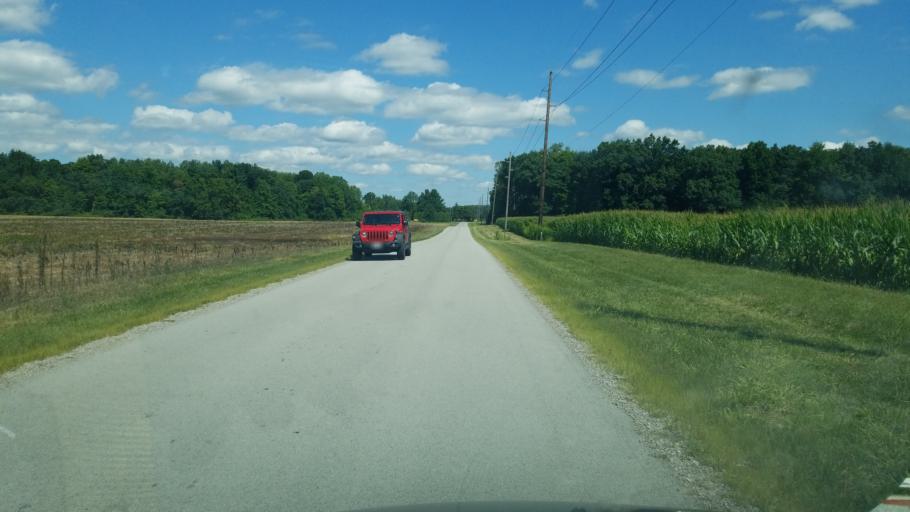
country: US
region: Ohio
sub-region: Wood County
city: Weston
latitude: 41.4269
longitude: -83.8653
